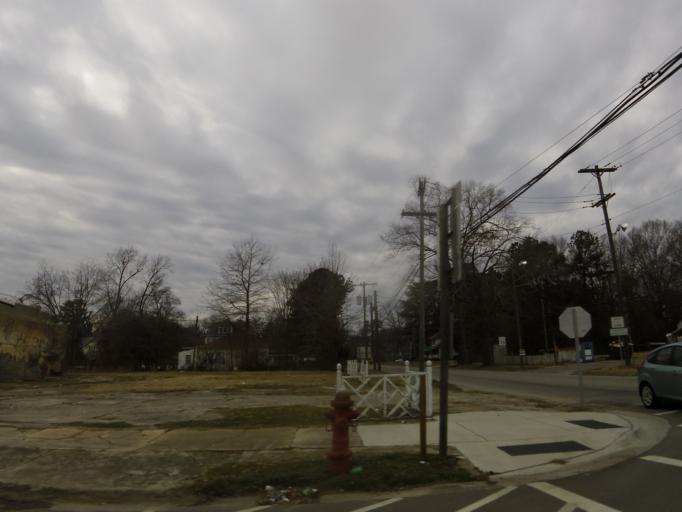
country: US
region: North Carolina
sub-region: Halifax County
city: Scotland Neck
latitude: 36.1319
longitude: -77.4232
